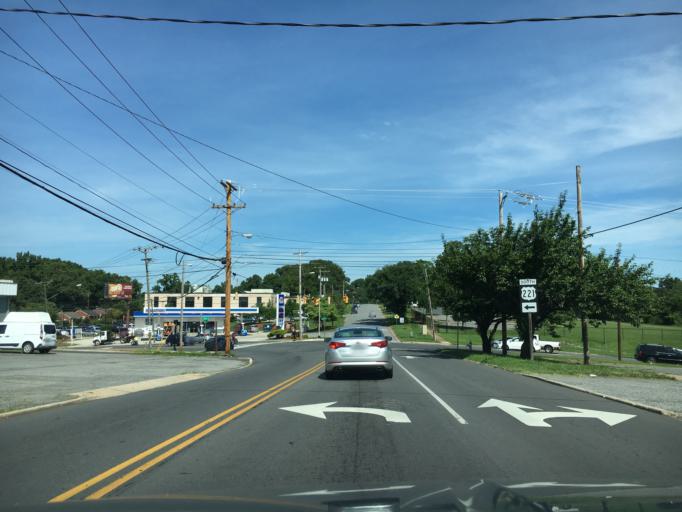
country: US
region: Virginia
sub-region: City of Lynchburg
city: West Lynchburg
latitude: 37.4028
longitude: -79.1775
